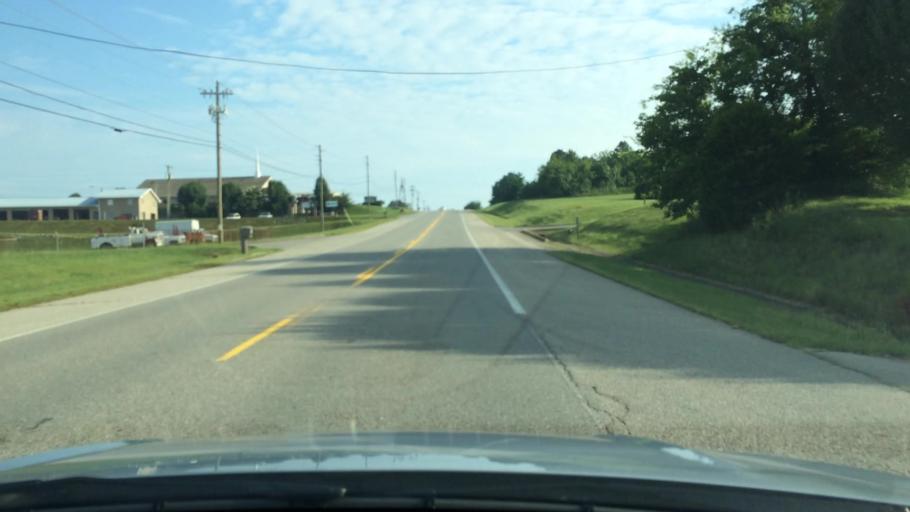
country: US
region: Tennessee
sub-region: Blount County
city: Louisville
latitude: 35.7499
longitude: -84.0443
